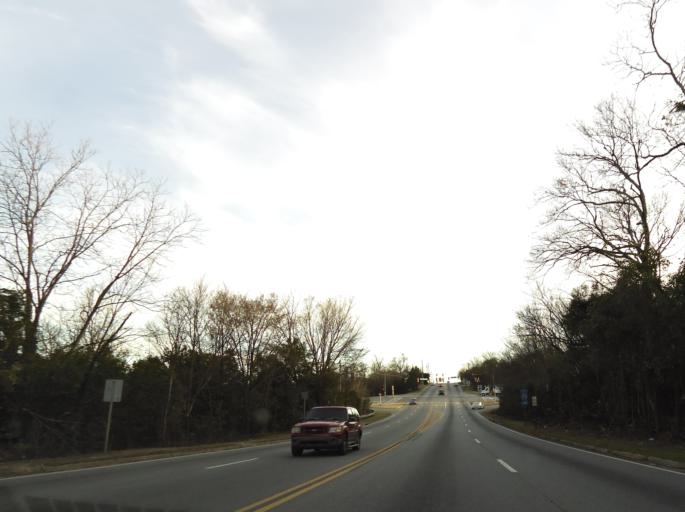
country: US
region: Georgia
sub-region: Bibb County
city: Macon
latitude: 32.8152
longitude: -83.6401
